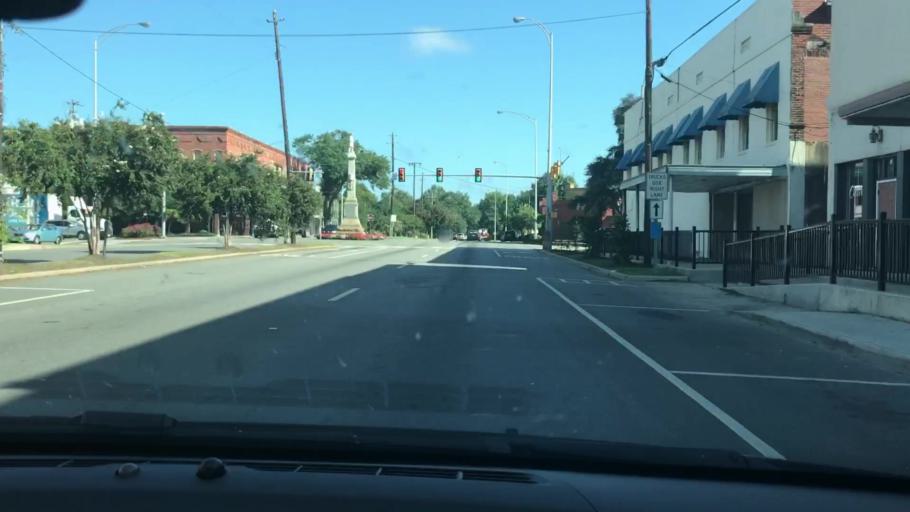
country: US
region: Alabama
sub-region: Barbour County
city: Eufaula
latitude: 31.8923
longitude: -85.1456
